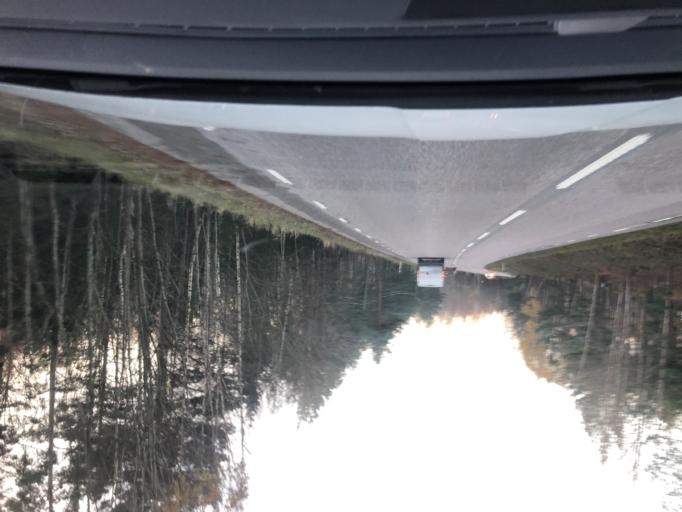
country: SE
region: Soedermanland
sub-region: Strangnas Kommun
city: Akers Styckebruk
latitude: 59.2970
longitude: 17.1015
